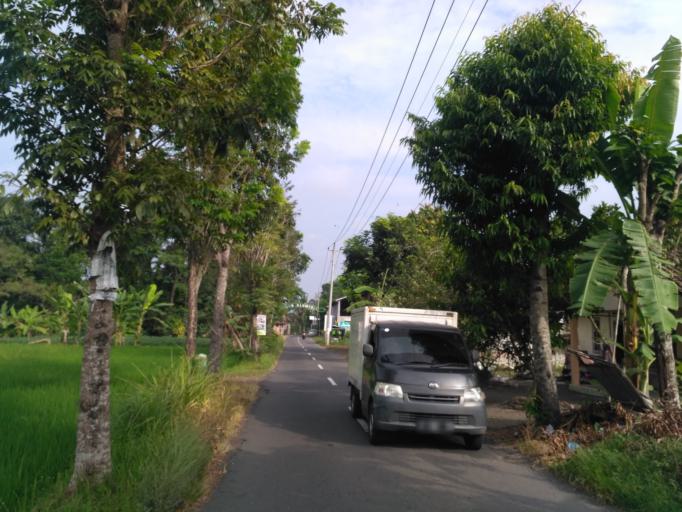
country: ID
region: Daerah Istimewa Yogyakarta
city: Melati
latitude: -7.7109
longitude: 110.3971
